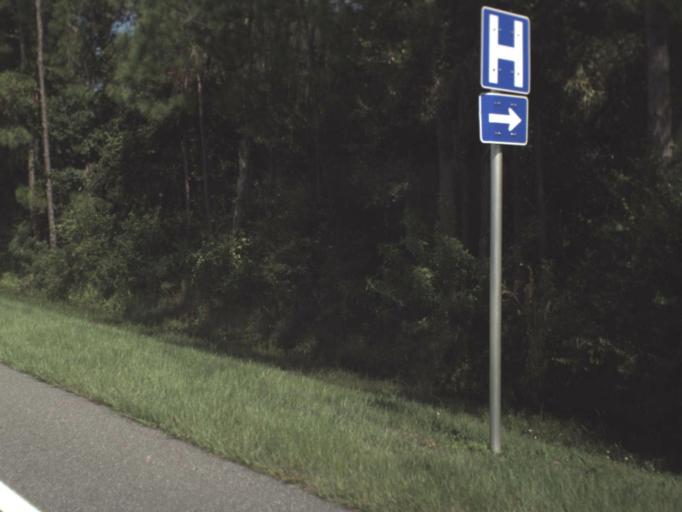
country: US
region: Florida
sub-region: Sarasota County
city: Lake Sarasota
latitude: 27.2575
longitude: -82.4005
